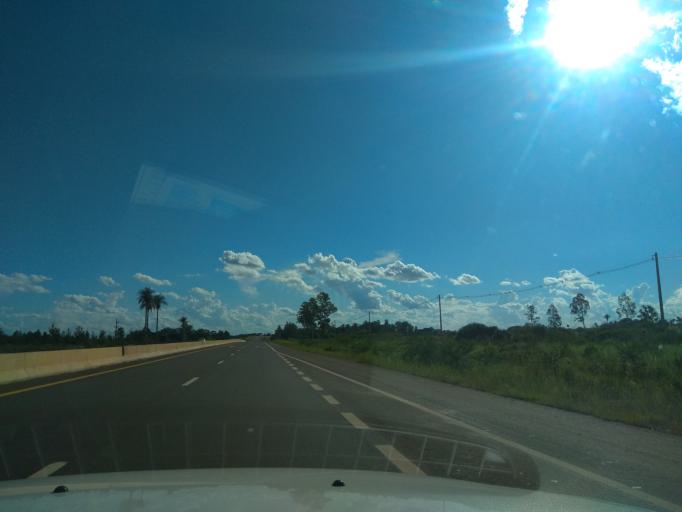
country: AR
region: Misiones
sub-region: Departamento de Candelaria
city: Candelaria
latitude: -27.4671
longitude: -55.7151
